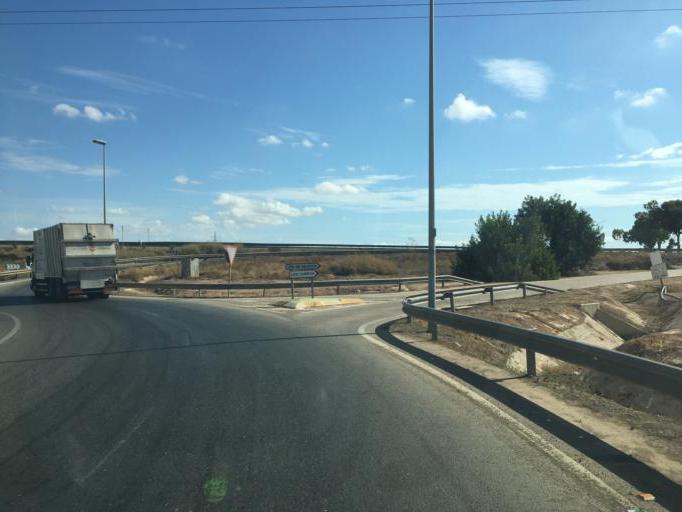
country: ES
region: Murcia
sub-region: Murcia
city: Cartagena
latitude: 37.6560
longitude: -0.9819
